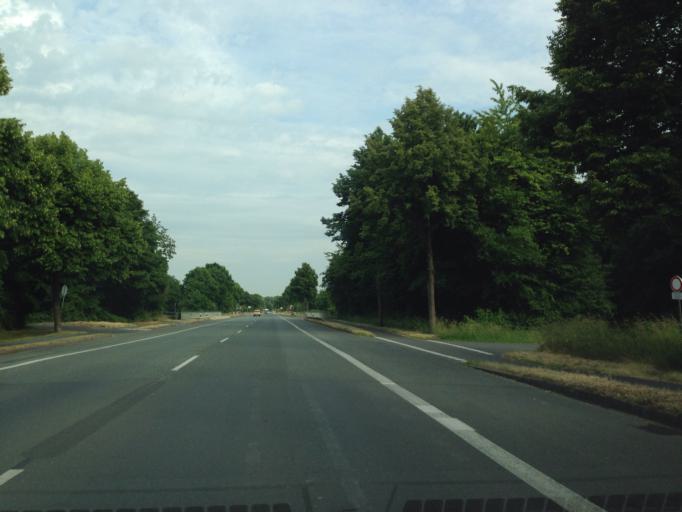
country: DE
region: North Rhine-Westphalia
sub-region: Regierungsbezirk Munster
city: Muenster
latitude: 51.9966
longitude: 7.5652
